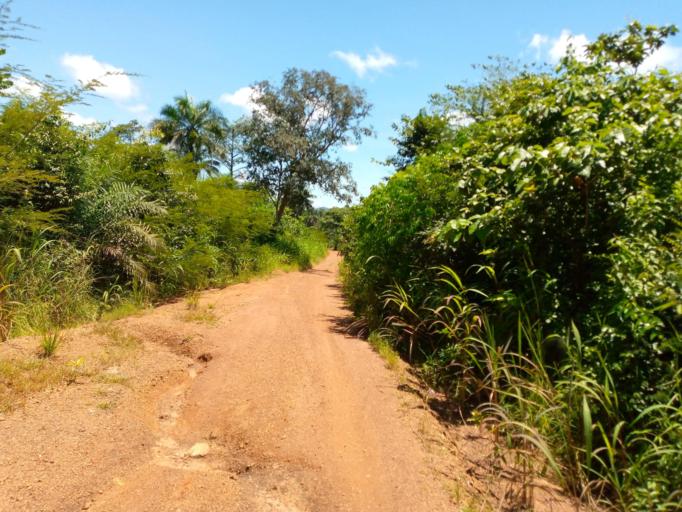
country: SL
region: Northern Province
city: Binkolo
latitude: 9.1172
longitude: -12.1738
